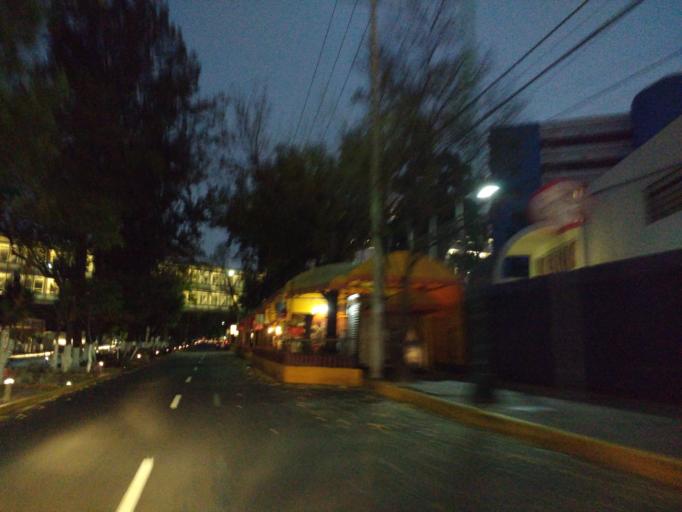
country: MX
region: Mexico City
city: Tlalpan
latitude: 19.2888
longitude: -99.1605
